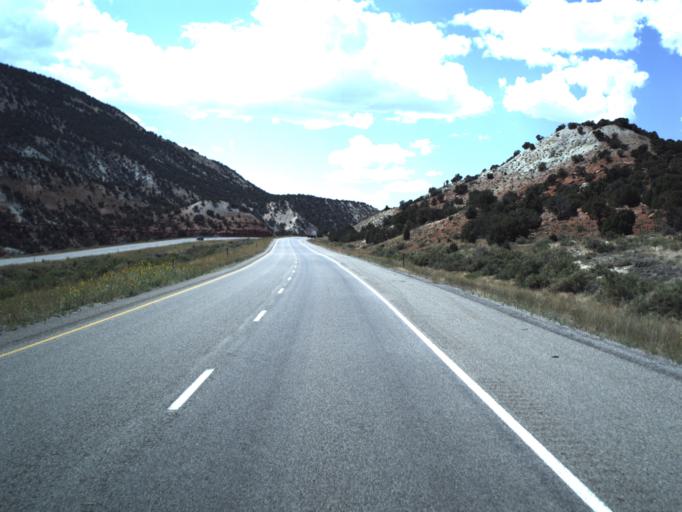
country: US
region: Utah
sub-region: Sevier County
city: Salina
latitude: 38.9251
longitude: -111.7739
